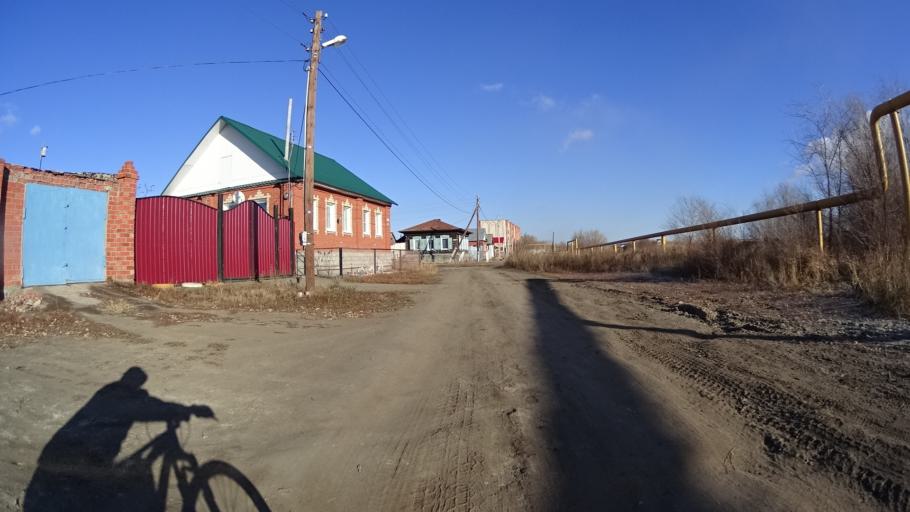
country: RU
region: Chelyabinsk
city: Troitsk
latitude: 54.0826
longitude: 61.5711
